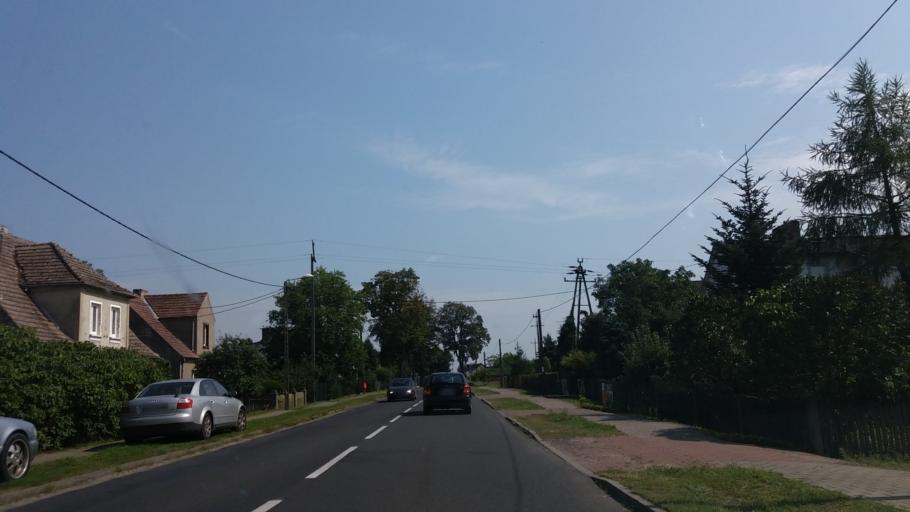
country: PL
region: Lubusz
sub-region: Powiat strzelecko-drezdenecki
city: Zwierzyn
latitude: 52.8381
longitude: 15.5766
